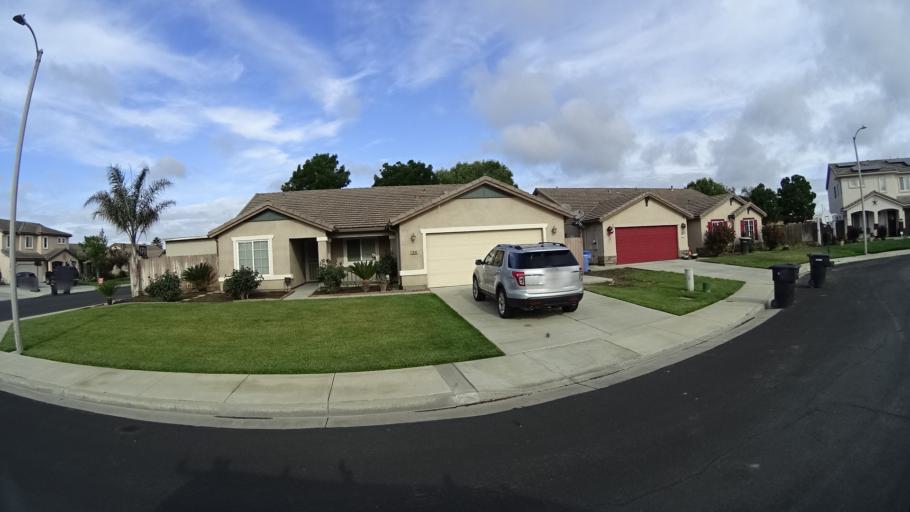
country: US
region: California
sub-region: Kings County
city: Lucerne
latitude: 36.3493
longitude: -119.6803
